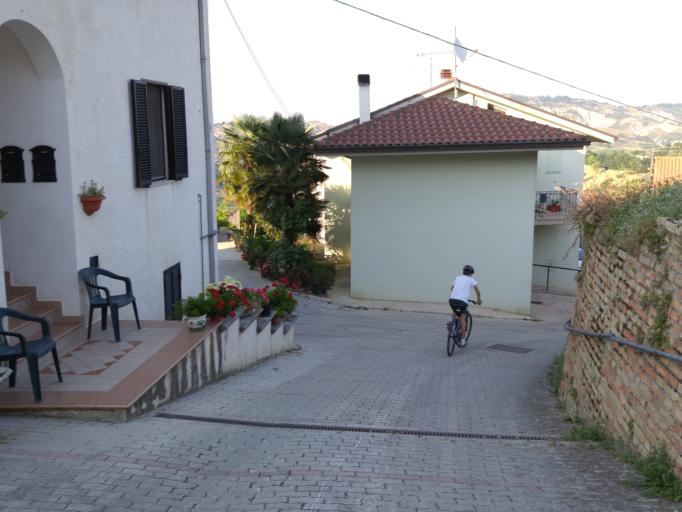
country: IT
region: Abruzzo
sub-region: Provincia di Teramo
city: Castilenti
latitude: 42.5605
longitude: 13.9209
